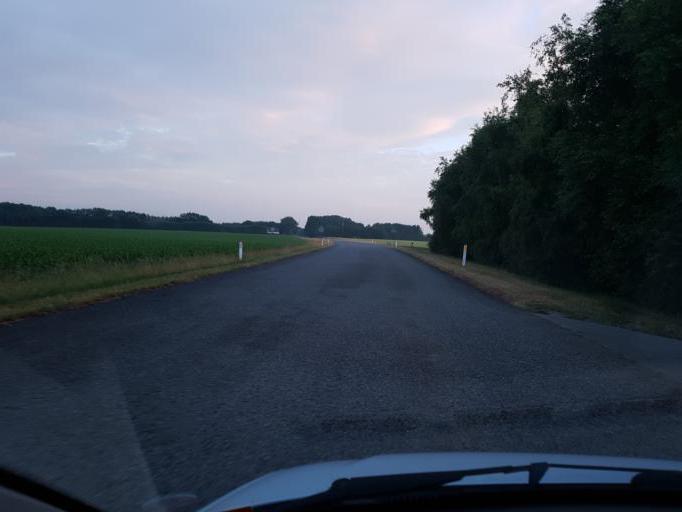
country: DK
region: South Denmark
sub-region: Esbjerg Kommune
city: Tjaereborg
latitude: 55.5211
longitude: 8.5732
